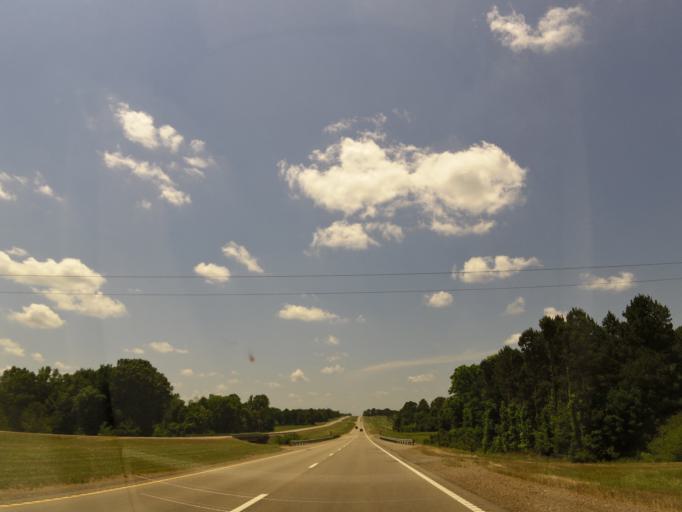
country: US
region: Mississippi
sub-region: Pontotoc County
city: Pontotoc
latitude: 34.2861
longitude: -89.1629
